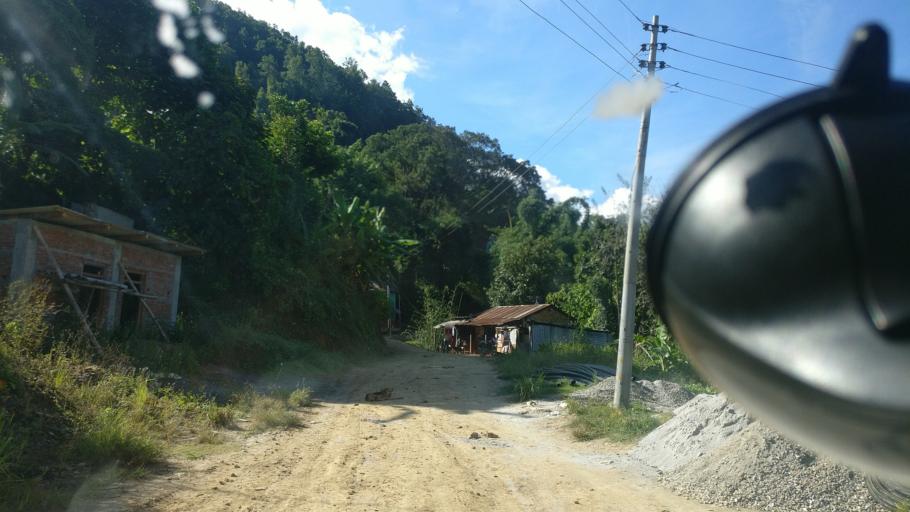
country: NP
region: Western Region
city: Baglung
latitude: 28.1442
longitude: 83.6465
